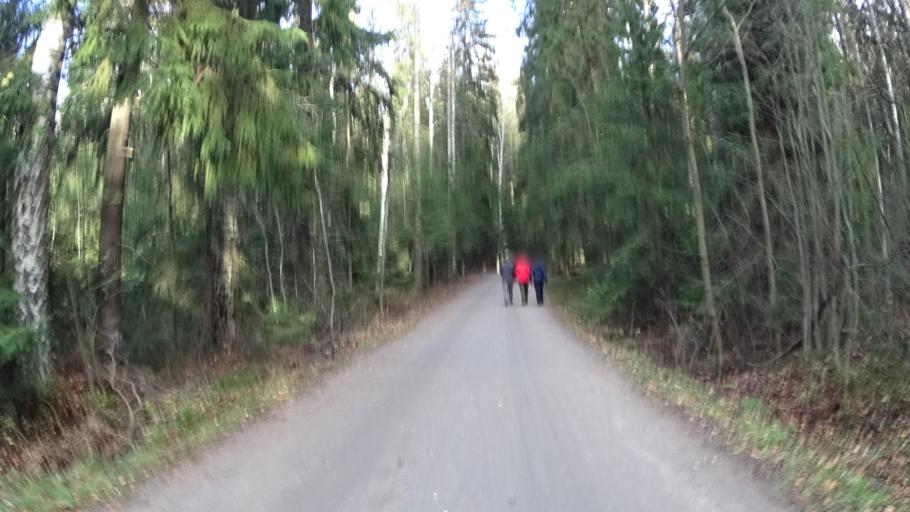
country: FI
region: Uusimaa
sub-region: Helsinki
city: Teekkarikylae
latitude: 60.2676
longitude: 24.9015
